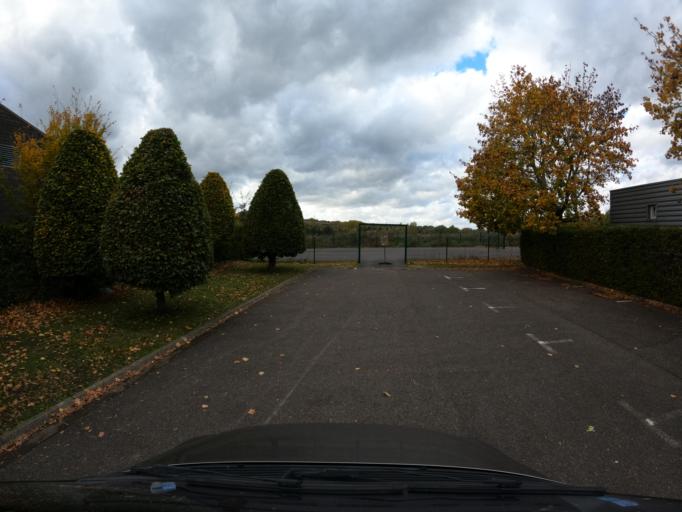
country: FR
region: Ile-de-France
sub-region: Departement de Seine-et-Marne
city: Coupvray
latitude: 48.8987
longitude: 2.7866
